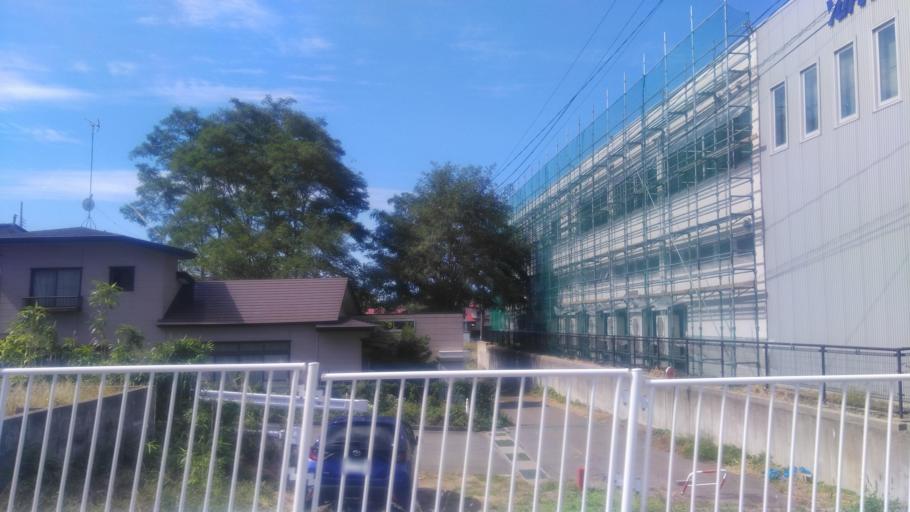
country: JP
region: Akita
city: Noshiromachi
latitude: 40.1957
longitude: 140.0226
